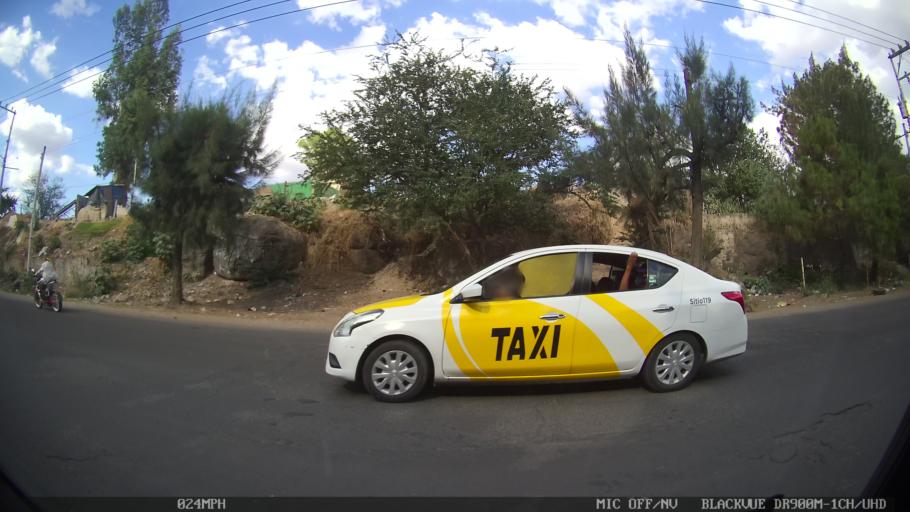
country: MX
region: Jalisco
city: Tlaquepaque
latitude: 20.6597
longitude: -103.2680
